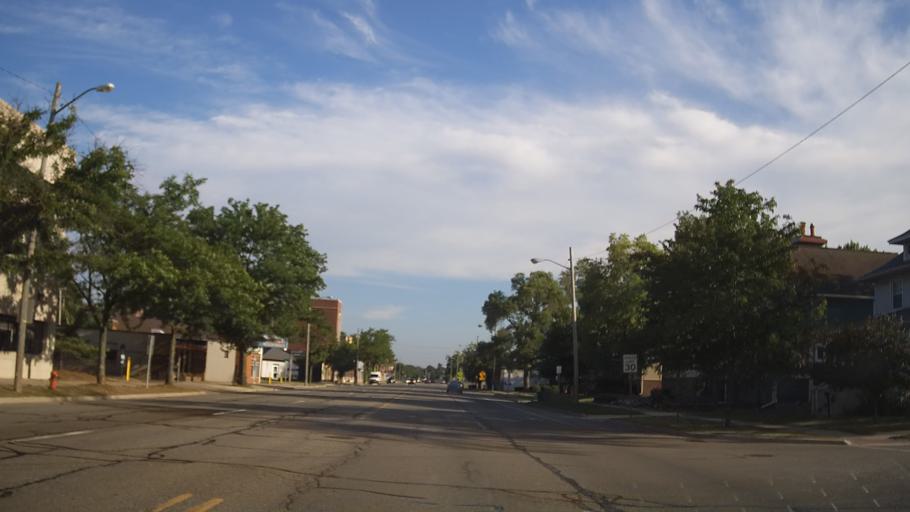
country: US
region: Michigan
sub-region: Oakland County
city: Royal Oak
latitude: 42.4824
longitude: -83.1466
